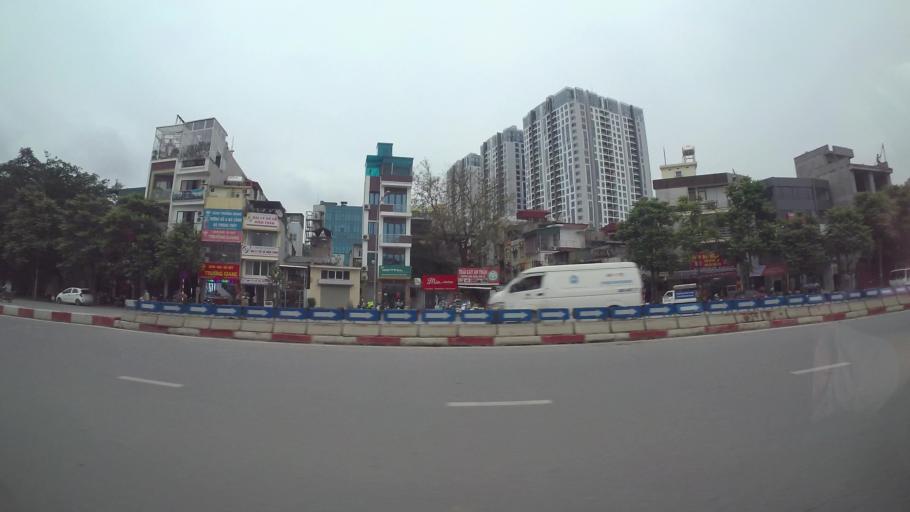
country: VN
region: Ha Noi
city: Hai BaTrung
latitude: 21.0087
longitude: 105.8631
